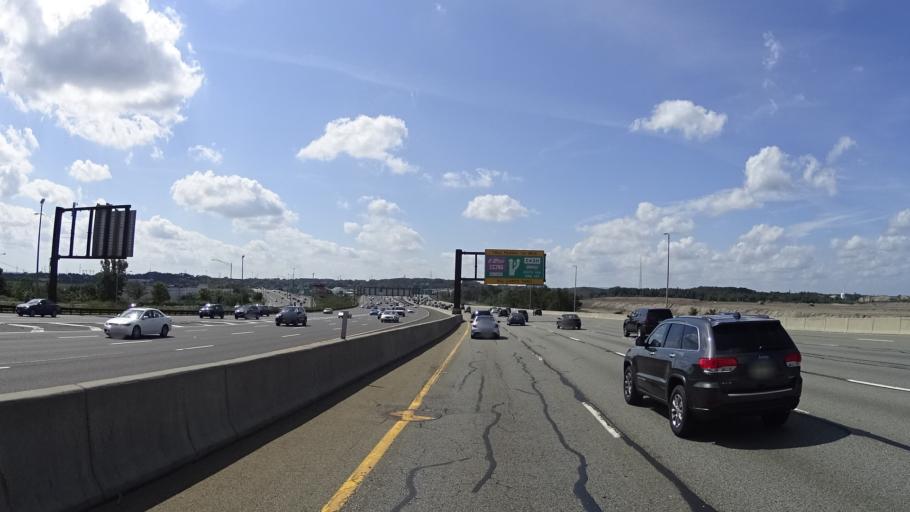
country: US
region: New Jersey
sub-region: Middlesex County
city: South Amboy
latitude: 40.5030
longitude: -74.3016
